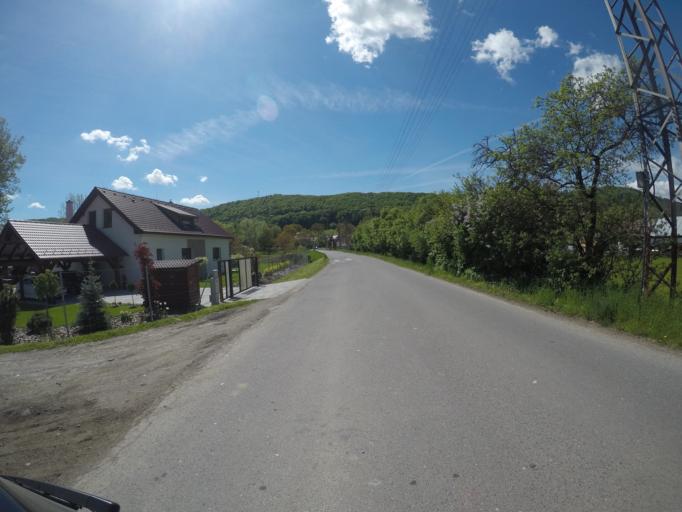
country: SK
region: Banskobystricky
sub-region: Okres Banska Bystrica
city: Banska Bystrica
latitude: 48.7410
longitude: 19.2173
